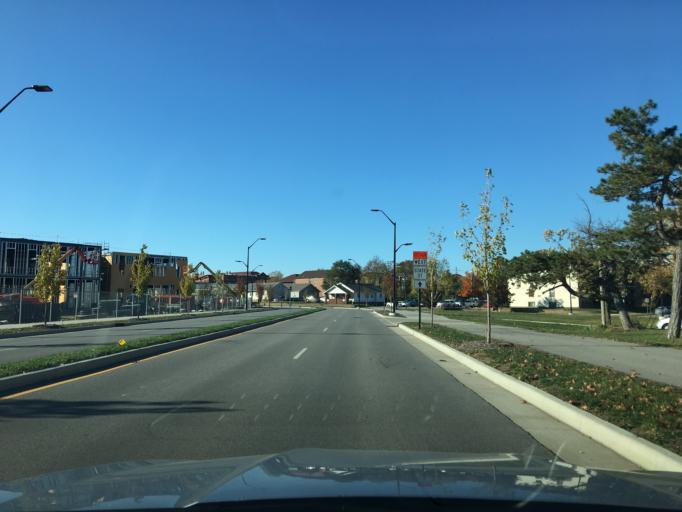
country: US
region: Indiana
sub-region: Tippecanoe County
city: West Lafayette
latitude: 40.4194
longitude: -86.9119
